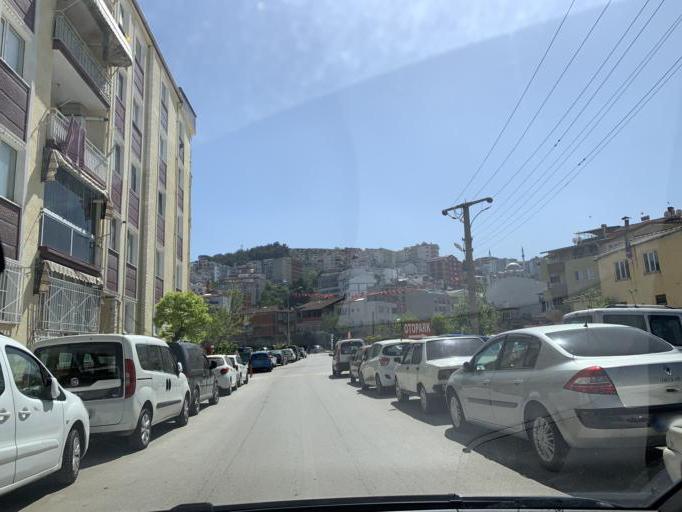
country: TR
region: Bursa
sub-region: Mudanya
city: Mudanya
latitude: 40.3542
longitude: 28.9289
